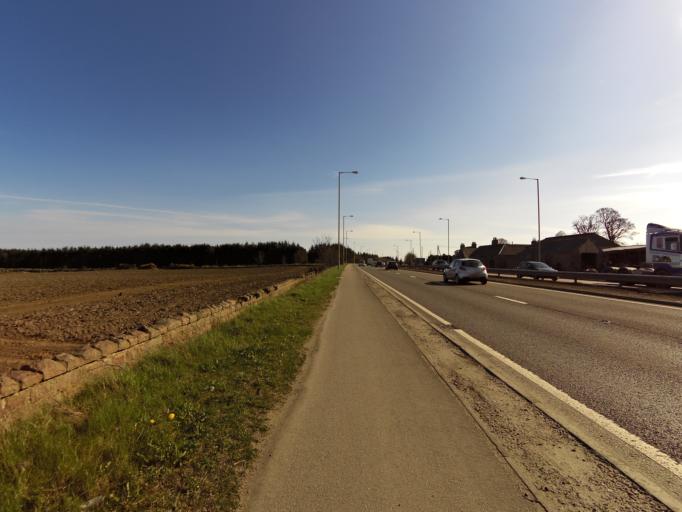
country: GB
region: Scotland
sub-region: Aberdeenshire
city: Newtonhill
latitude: 57.0509
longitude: -2.1501
